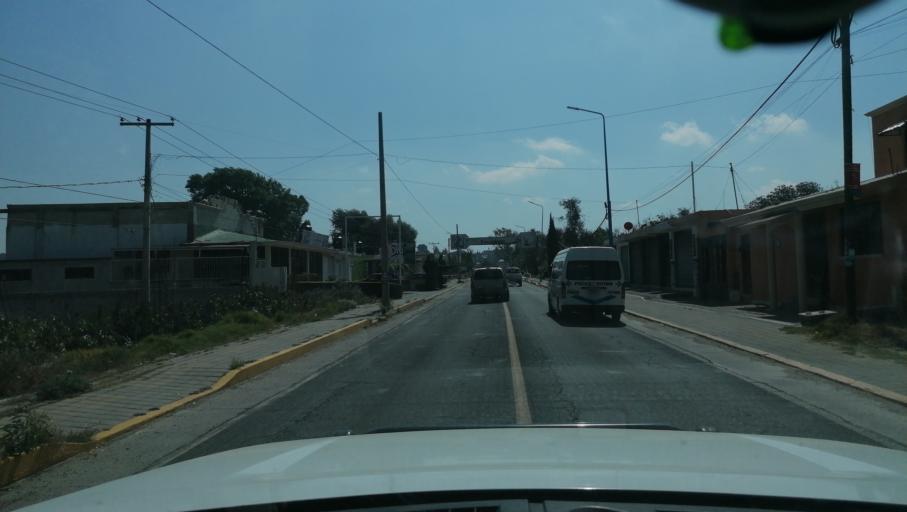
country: MX
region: Tlaxcala
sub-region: San Jeronimo Zacualpan
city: San Jeronimo Zacualpan
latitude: 19.2397
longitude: -98.2594
